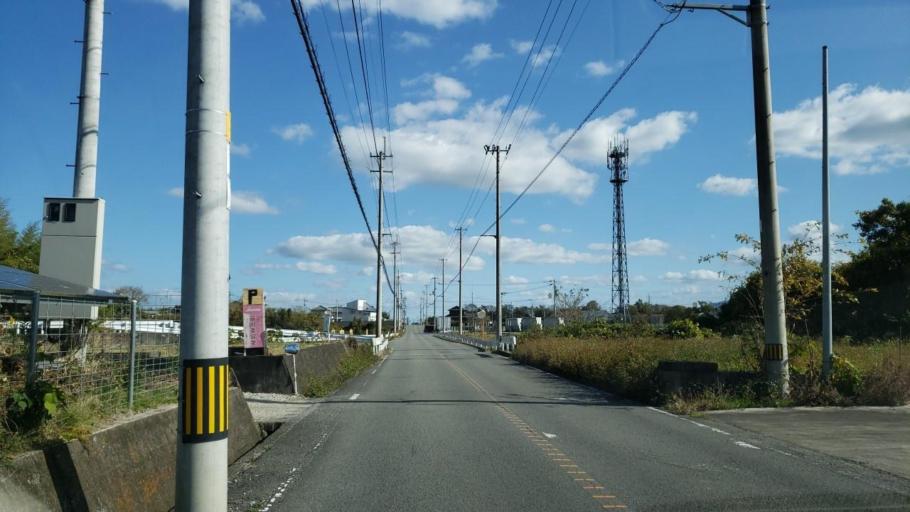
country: JP
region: Tokushima
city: Wakimachi
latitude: 34.0818
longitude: 134.2150
